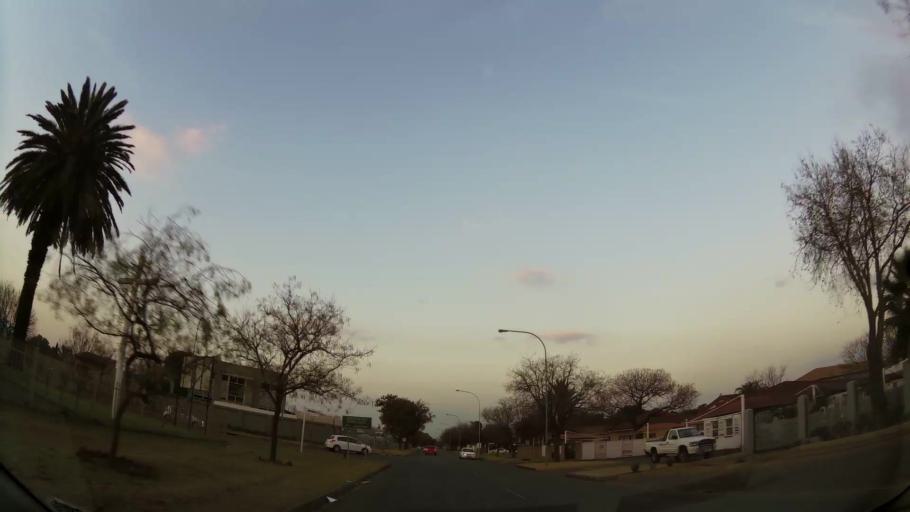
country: ZA
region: Gauteng
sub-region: Ekurhuleni Metropolitan Municipality
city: Benoni
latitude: -26.1640
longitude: 28.3202
